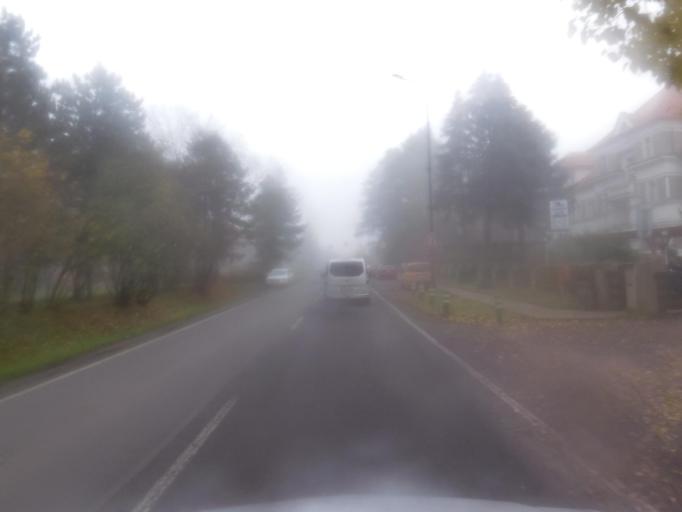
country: CZ
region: Ustecky
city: Libochovice
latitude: 50.4032
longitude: 14.0343
